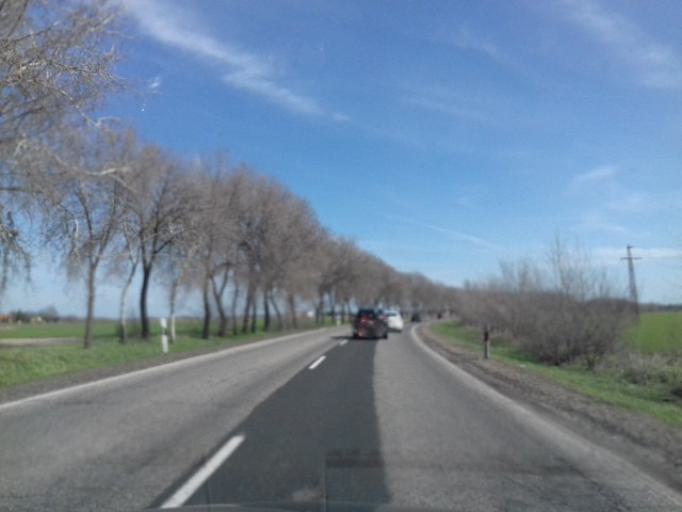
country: HU
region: Bacs-Kiskun
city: Nyarlorinc
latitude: 46.9151
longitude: 19.7986
